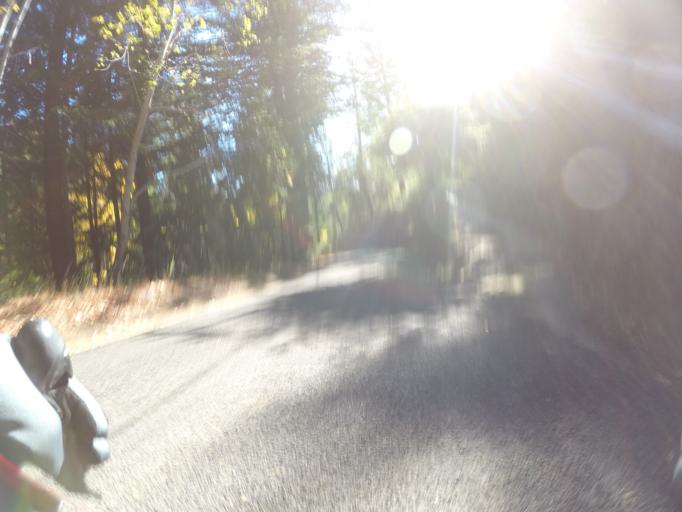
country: US
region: California
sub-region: Santa Cruz County
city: Lompico
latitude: 37.1249
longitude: -122.0194
